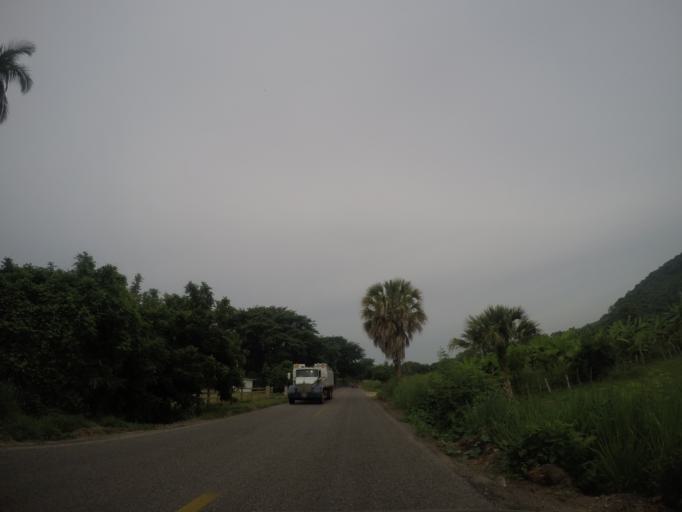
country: MX
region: Oaxaca
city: San Pedro Mixtepec
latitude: 15.9458
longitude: -97.1818
